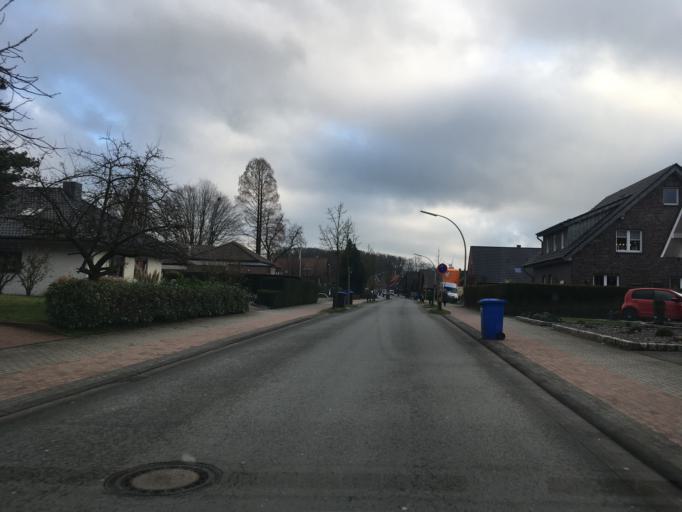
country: DE
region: North Rhine-Westphalia
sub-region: Regierungsbezirk Munster
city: Gescher
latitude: 51.9510
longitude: 6.9974
